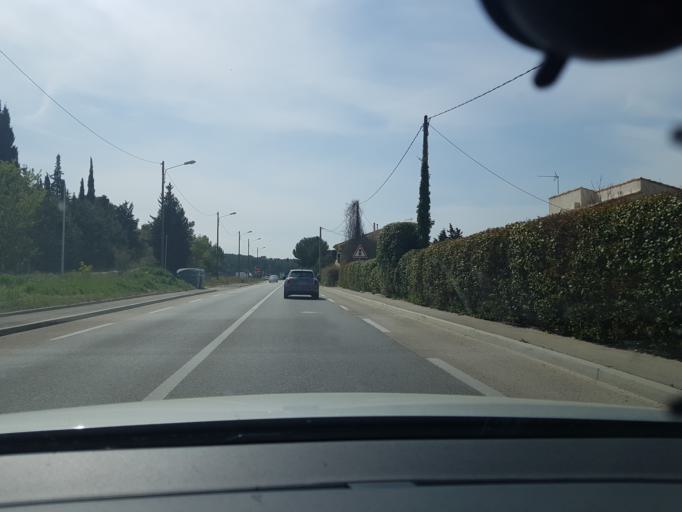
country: FR
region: Provence-Alpes-Cote d'Azur
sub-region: Departement des Bouches-du-Rhone
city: Bouc-Bel-Air
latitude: 43.4730
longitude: 5.4099
